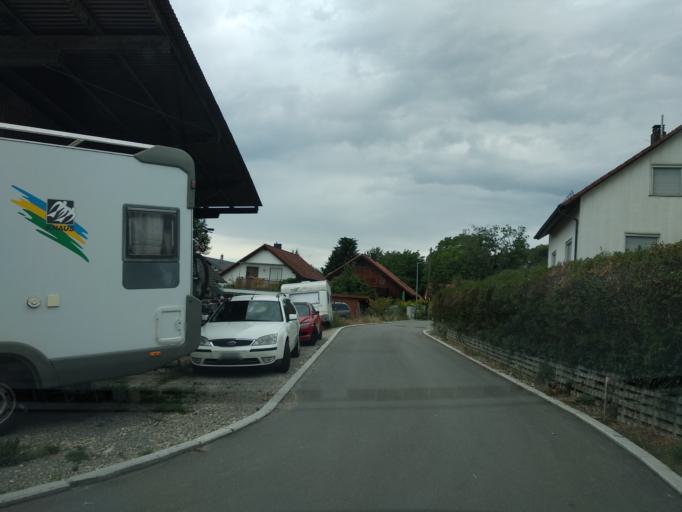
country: DE
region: Baden-Wuerttemberg
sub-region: Freiburg Region
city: Gailingen
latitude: 47.6973
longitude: 8.7504
